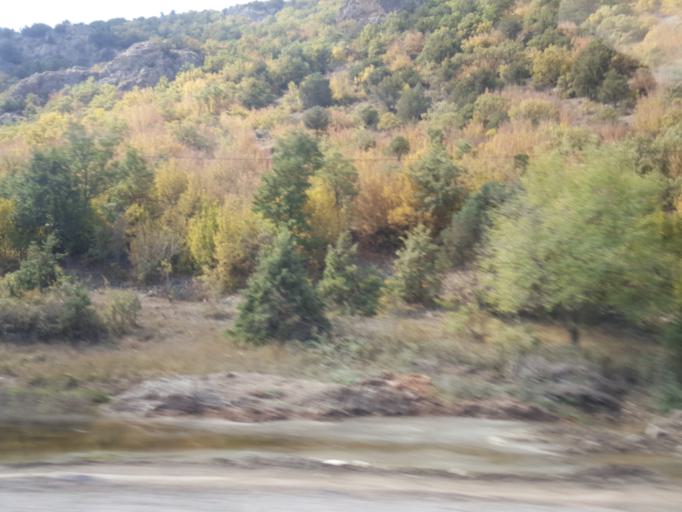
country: TR
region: Yozgat
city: Cekerek
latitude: 40.1127
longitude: 35.6159
